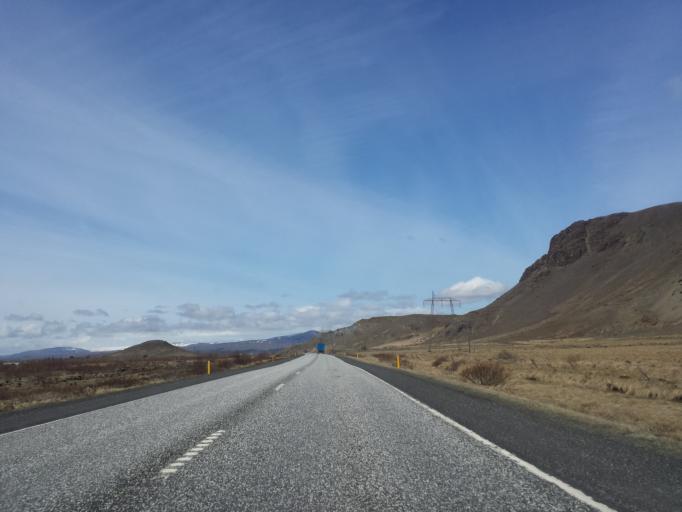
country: IS
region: South
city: Selfoss
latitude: 63.9553
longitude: -21.0471
